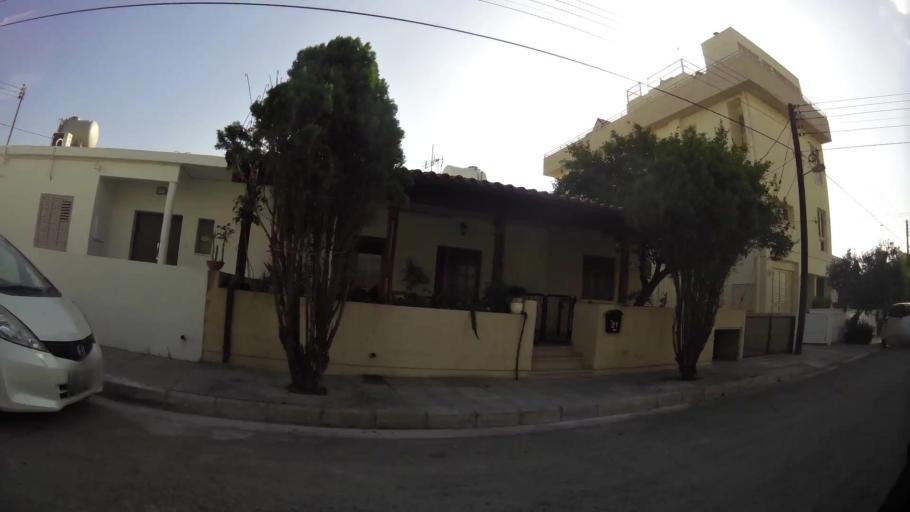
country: CY
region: Lefkosia
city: Nicosia
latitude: 35.1804
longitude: 33.3310
